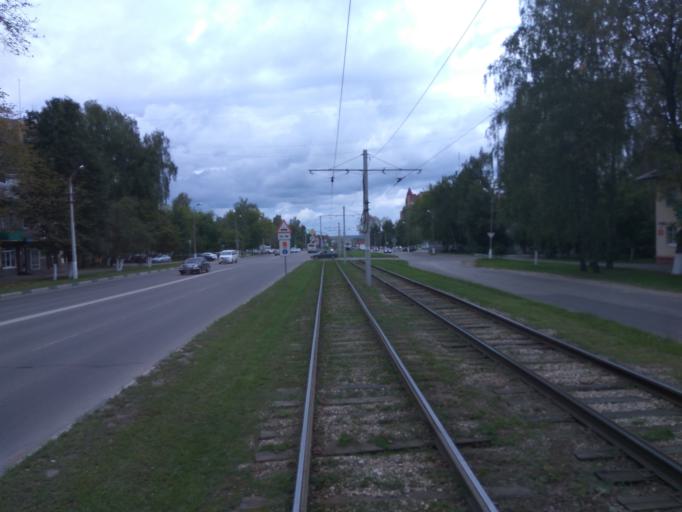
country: RU
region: Moskovskaya
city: Kolomna
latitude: 55.0818
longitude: 38.7630
